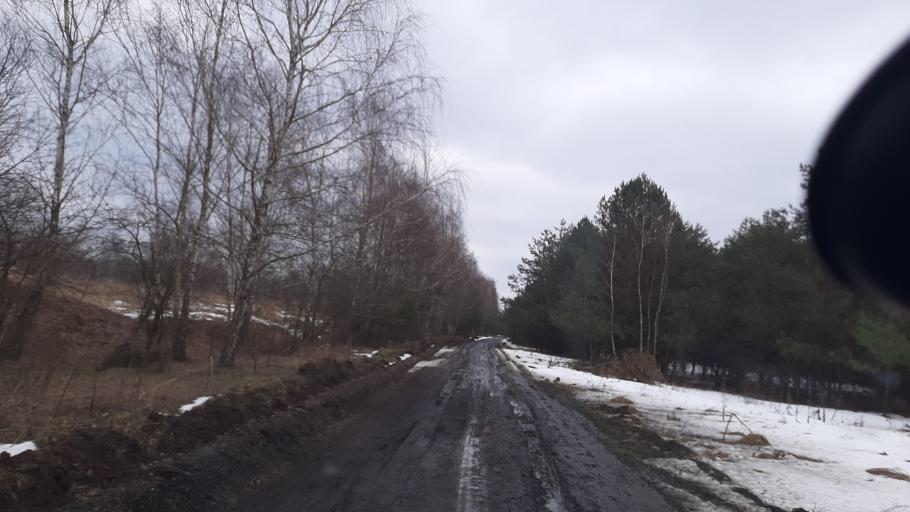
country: PL
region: Lublin Voivodeship
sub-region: Powiat wlodawski
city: Wlodawa
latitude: 51.5149
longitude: 23.6067
